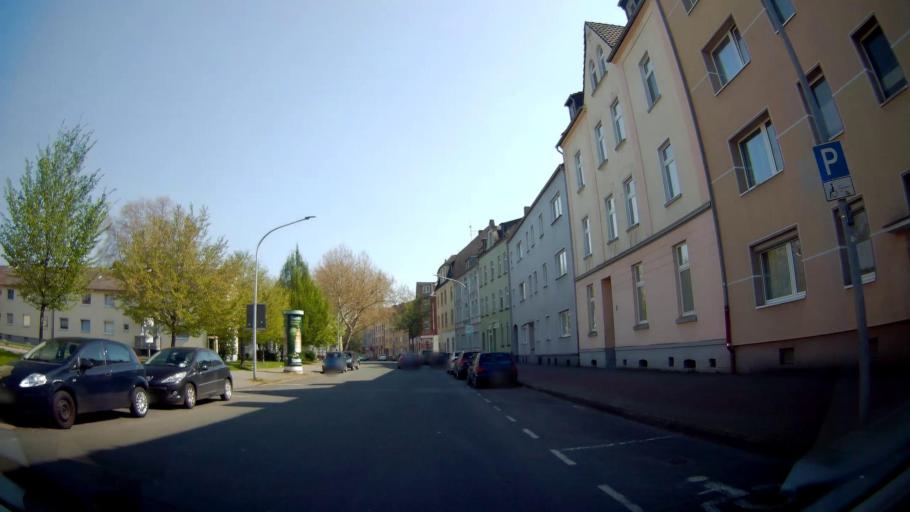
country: DE
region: North Rhine-Westphalia
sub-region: Regierungsbezirk Munster
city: Gelsenkirchen
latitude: 51.5313
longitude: 7.1189
